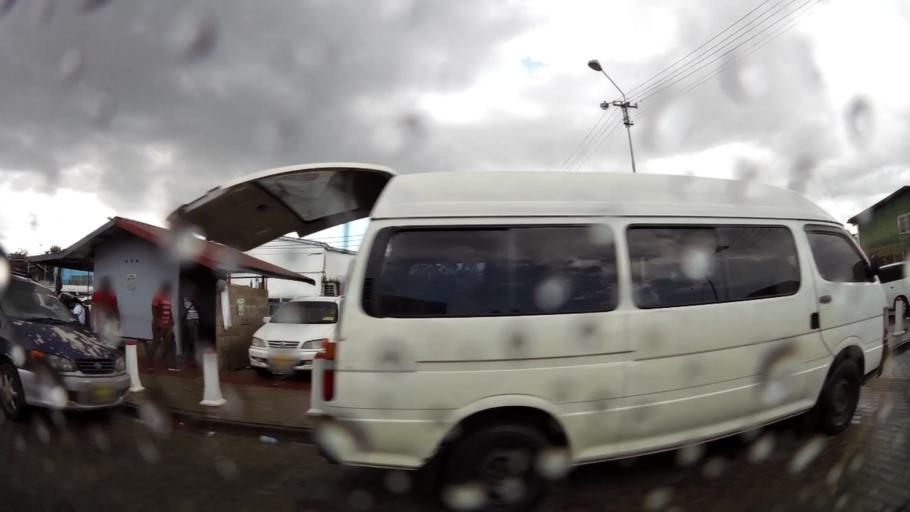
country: SR
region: Paramaribo
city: Paramaribo
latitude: 5.8235
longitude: -55.1678
